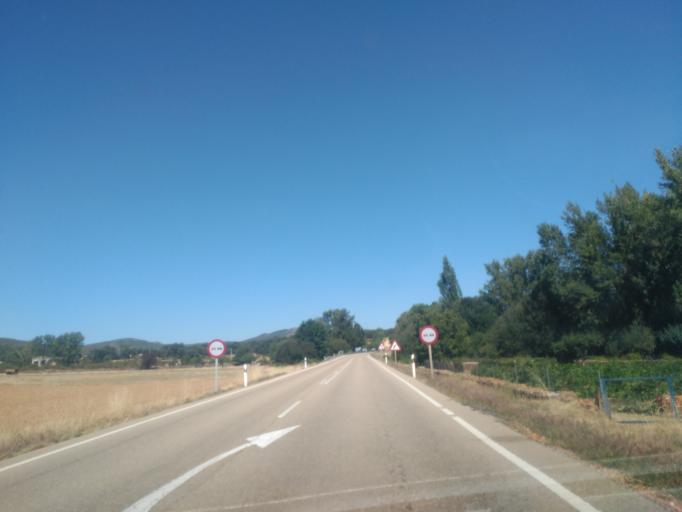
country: ES
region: Castille and Leon
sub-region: Provincia de Zamora
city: Tabara
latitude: 41.8342
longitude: -5.9702
